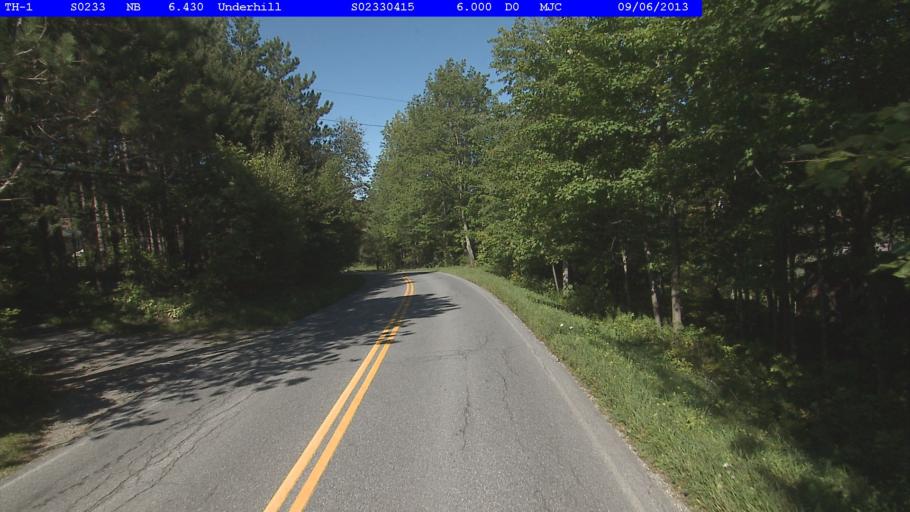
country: US
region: Vermont
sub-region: Chittenden County
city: Jericho
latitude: 44.5514
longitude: -72.8670
